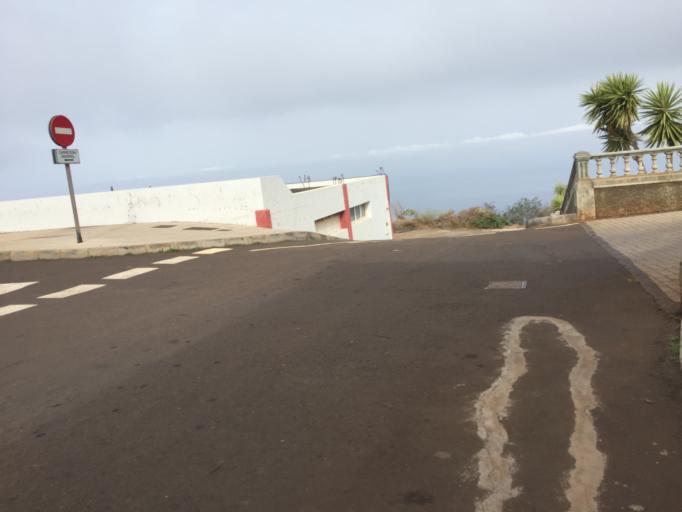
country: ES
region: Canary Islands
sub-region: Provincia de Santa Cruz de Tenerife
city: Garafia
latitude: 28.8301
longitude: -17.9454
